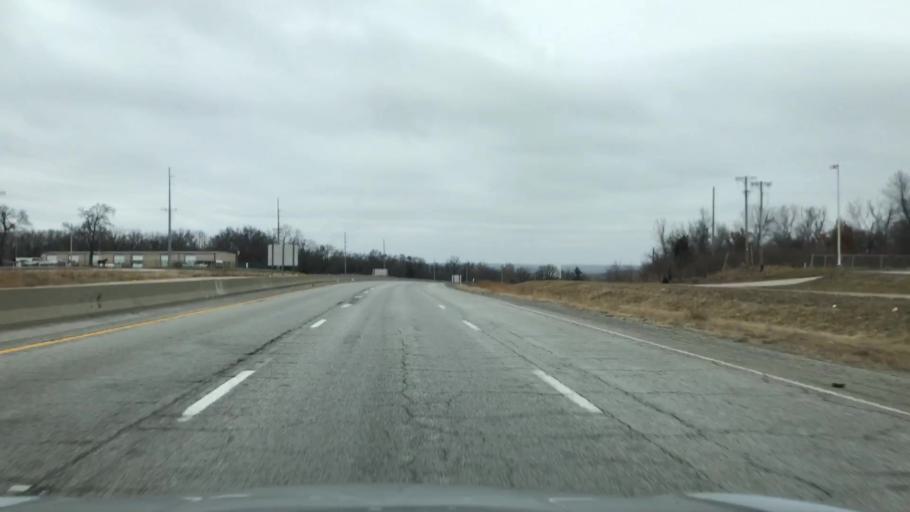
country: US
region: Missouri
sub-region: Jackson County
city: East Independence
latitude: 39.1194
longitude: -94.3857
